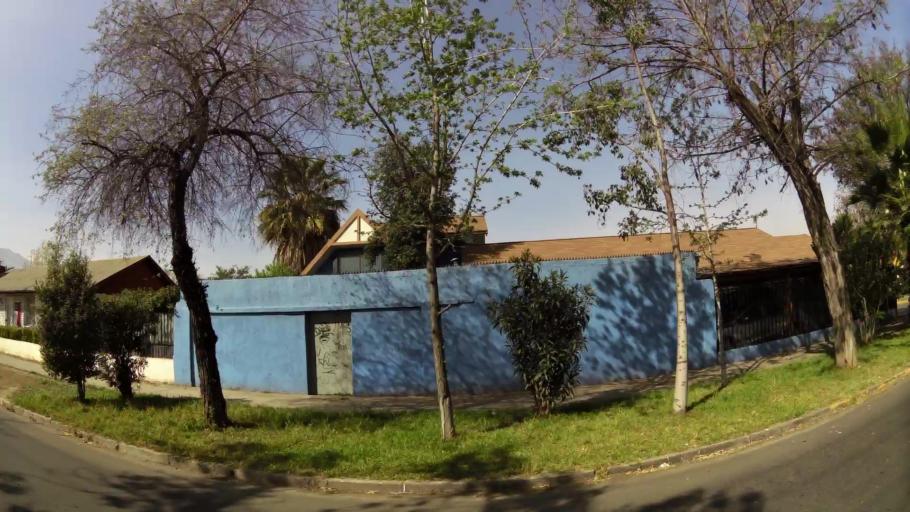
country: CL
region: Santiago Metropolitan
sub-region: Provincia de Santiago
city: Villa Presidente Frei, Nunoa, Santiago, Chile
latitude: -33.4913
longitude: -70.5919
